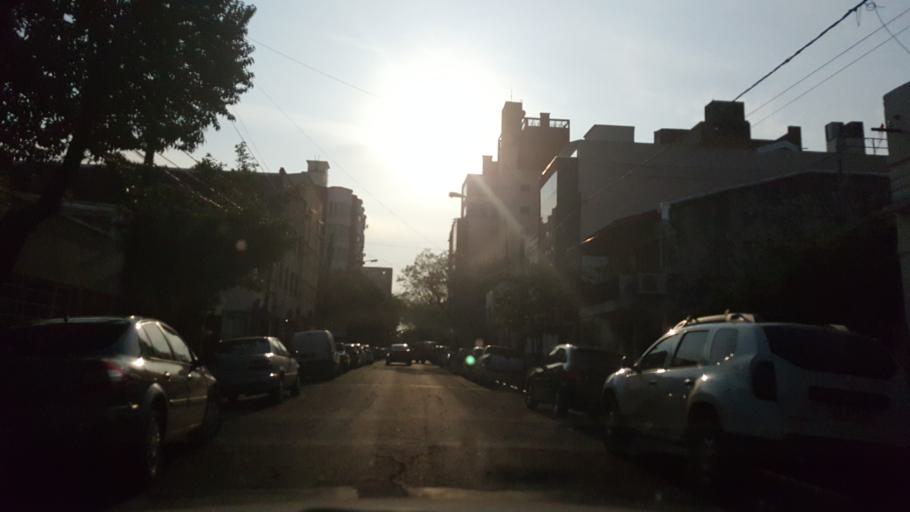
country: AR
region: Misiones
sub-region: Departamento de Capital
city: Posadas
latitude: -27.3693
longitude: -55.8898
